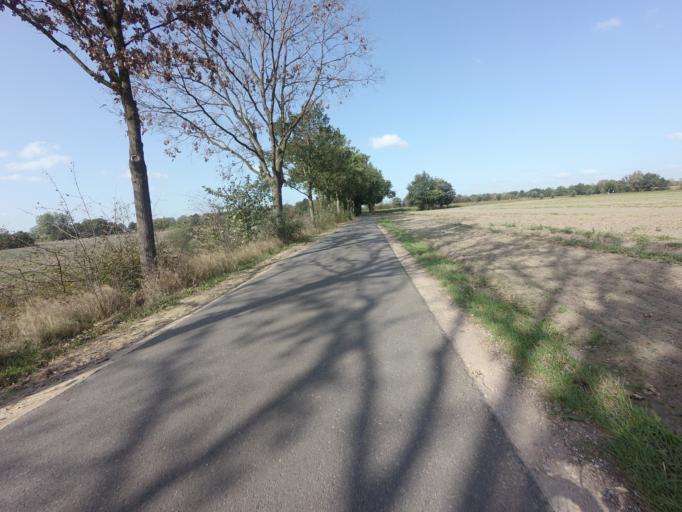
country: NL
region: Limburg
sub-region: Gemeente Roerdalen
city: Herkenbosch
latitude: 51.1926
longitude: 6.0601
